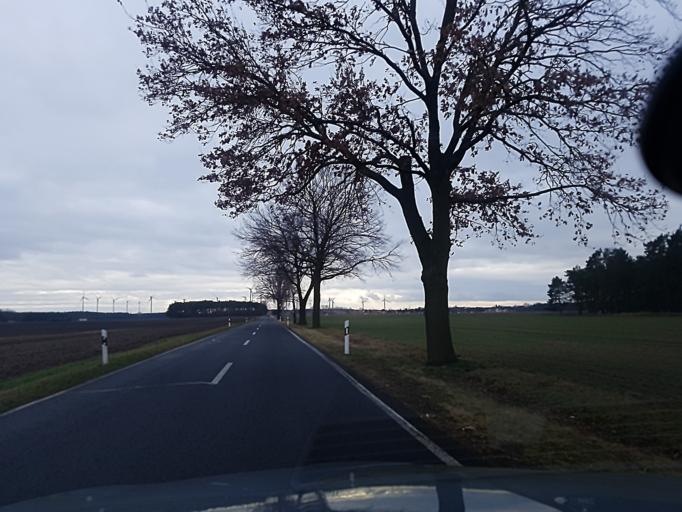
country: DE
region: Brandenburg
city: Schilda
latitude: 51.5578
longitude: 13.3396
